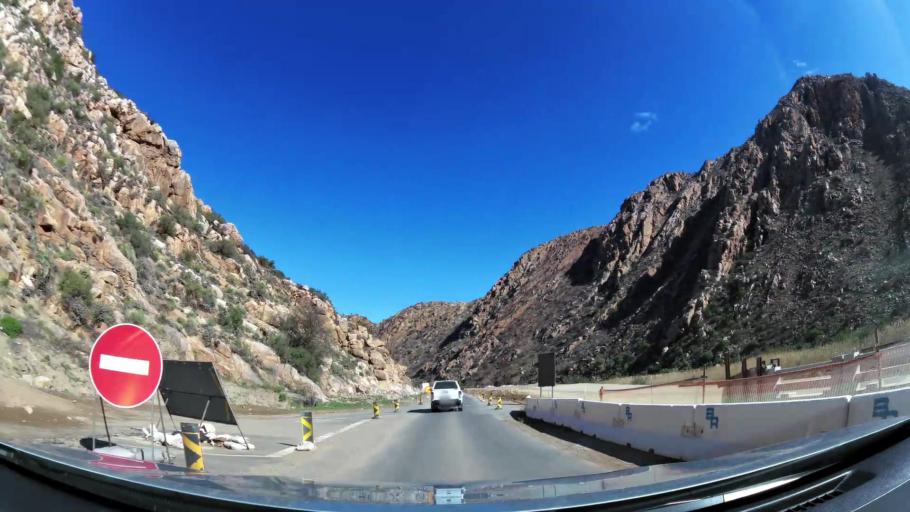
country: ZA
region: Western Cape
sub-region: Cape Winelands District Municipality
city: Ashton
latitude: -33.7939
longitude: 20.1054
